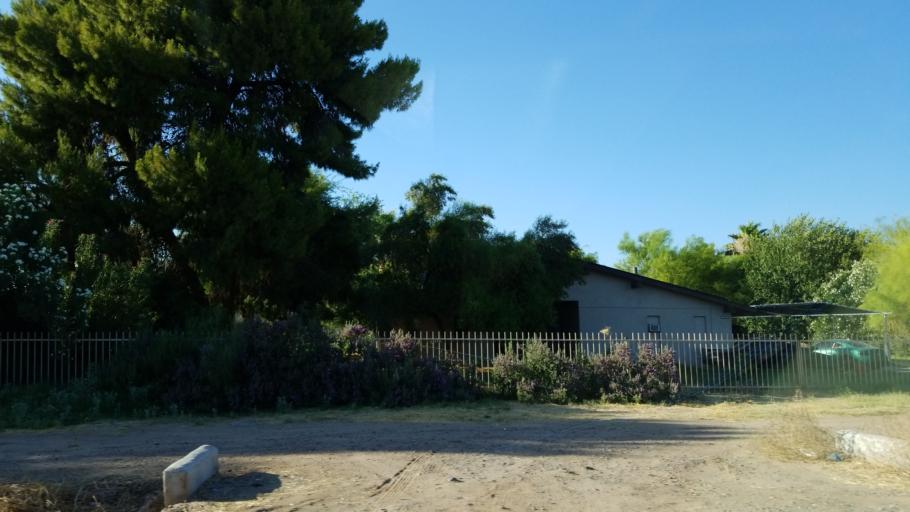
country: US
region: Arizona
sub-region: Maricopa County
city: Laveen
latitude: 33.3774
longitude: -112.2001
